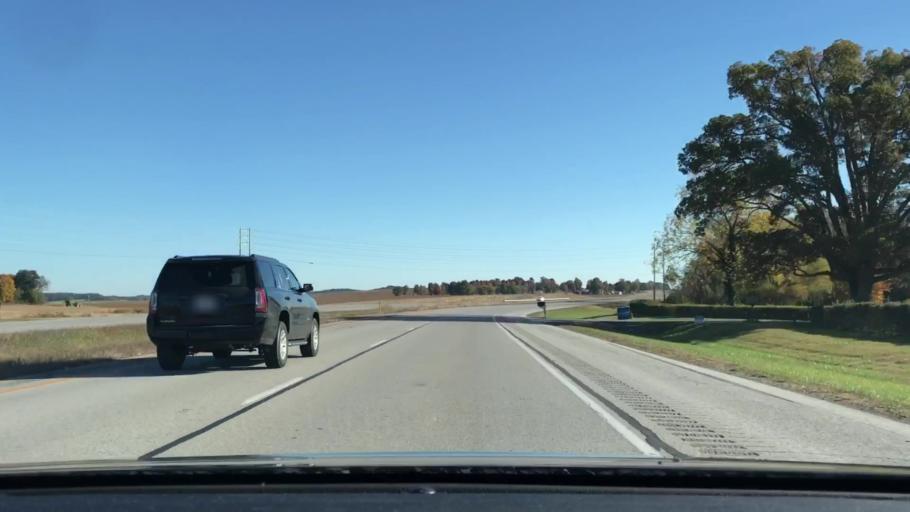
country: US
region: Kentucky
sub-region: Logan County
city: Auburn
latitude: 36.8738
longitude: -86.6832
